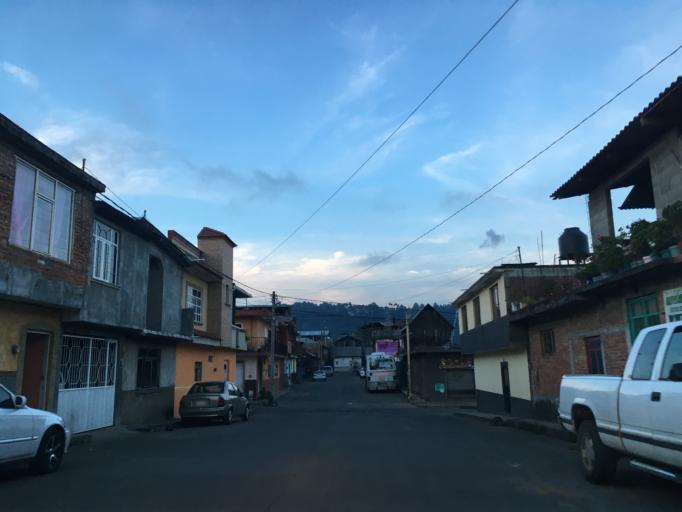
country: MX
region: Michoacan
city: Charapan
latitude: 19.6501
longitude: -102.2486
